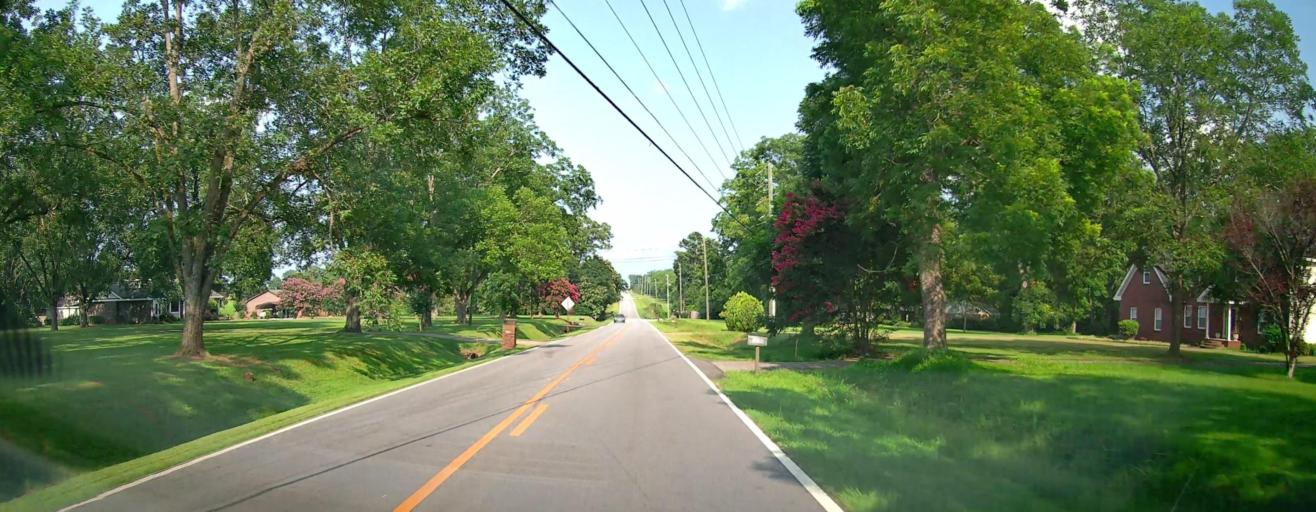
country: US
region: Georgia
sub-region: Houston County
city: Centerville
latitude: 32.6595
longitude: -83.6969
